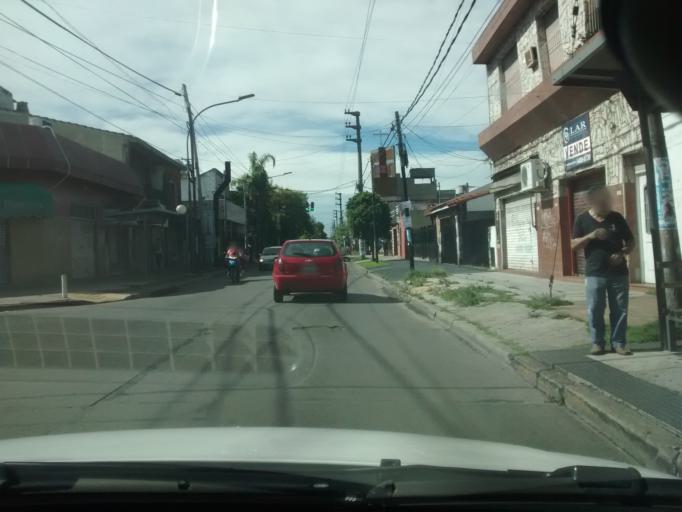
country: AR
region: Buenos Aires
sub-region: Partido de Moron
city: Moron
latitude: -34.6649
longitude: -58.6181
